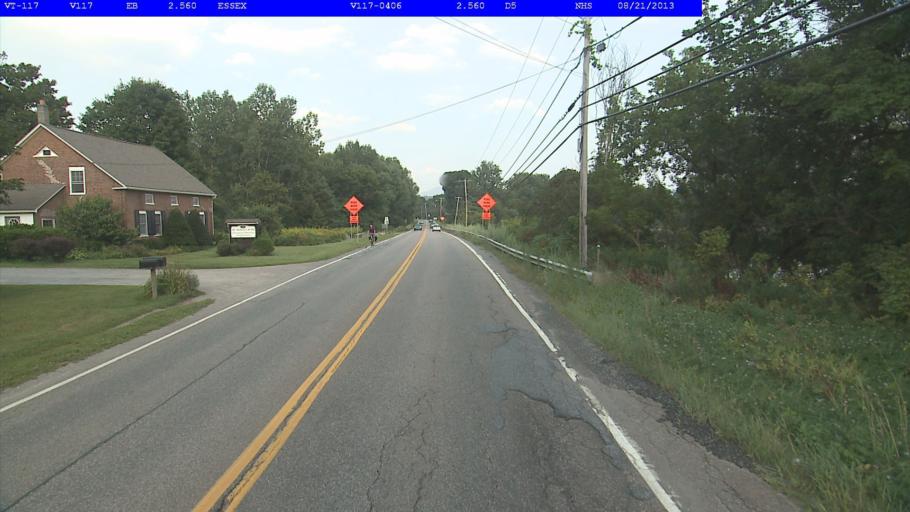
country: US
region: Vermont
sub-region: Chittenden County
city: Williston
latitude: 44.4796
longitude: -73.0638
